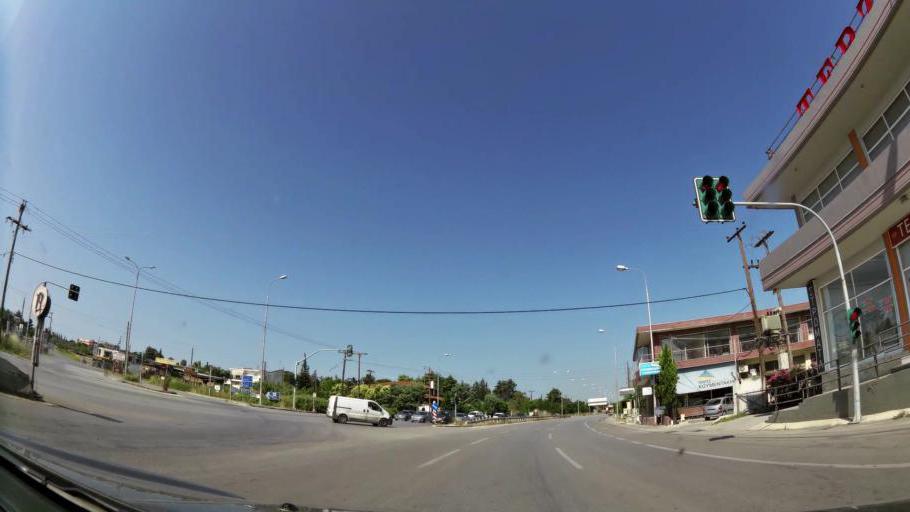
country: GR
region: Central Macedonia
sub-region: Nomos Thessalonikis
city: Neo Rysi
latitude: 40.5000
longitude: 22.9656
